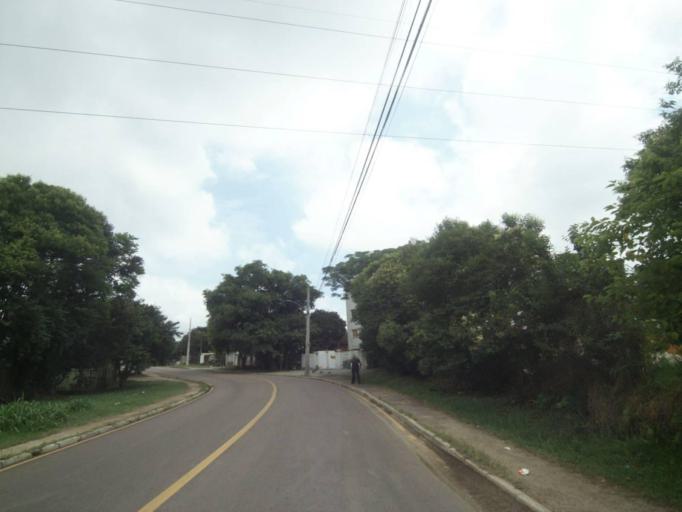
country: BR
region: Parana
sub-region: Curitiba
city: Curitiba
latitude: -25.4814
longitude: -49.3410
